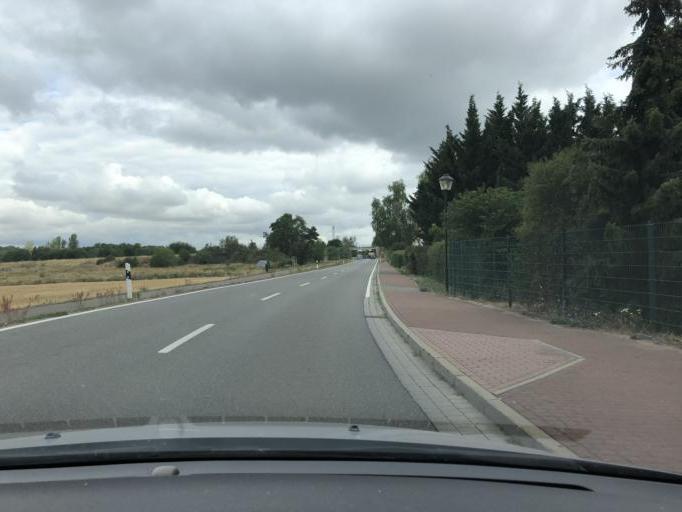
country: DE
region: Saxony-Anhalt
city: Lochau
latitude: 51.4000
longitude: 12.0456
